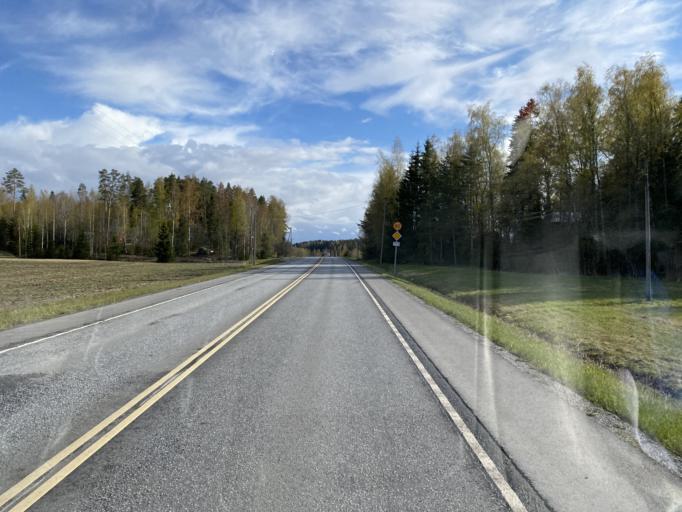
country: FI
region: Pirkanmaa
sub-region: Tampere
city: Lempaeaelae
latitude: 61.2638
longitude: 23.7442
